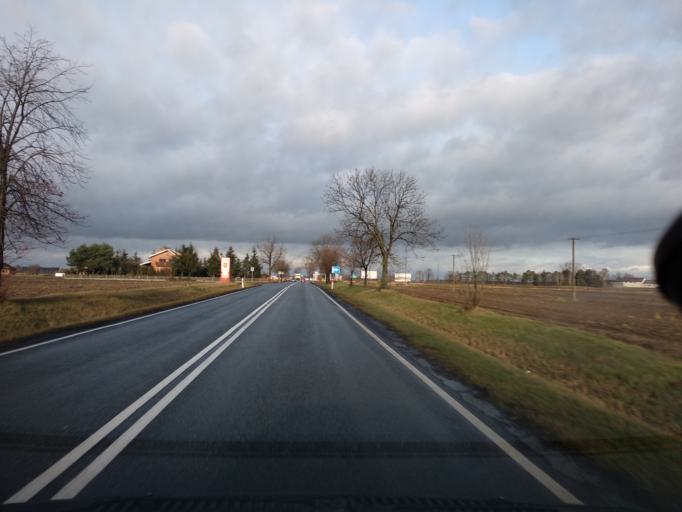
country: PL
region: Greater Poland Voivodeship
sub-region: Powiat koninski
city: Rychwal
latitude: 52.1015
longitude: 18.1669
